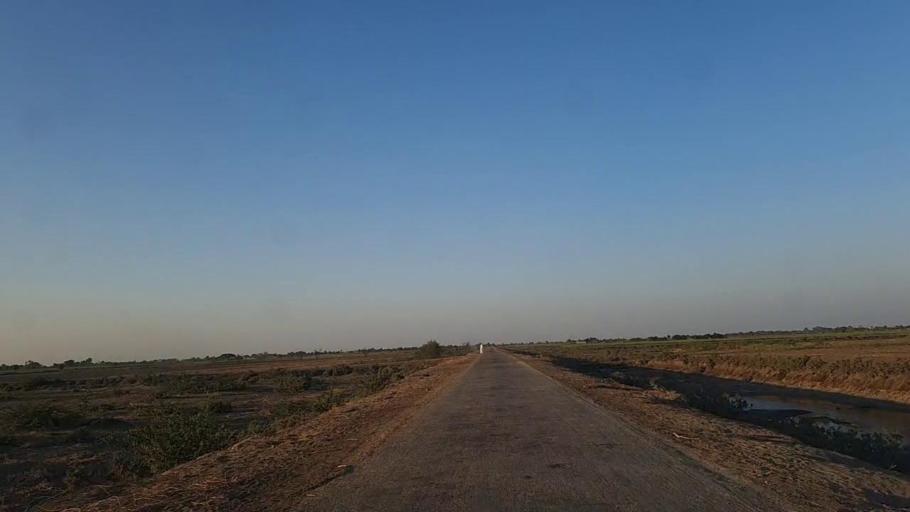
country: PK
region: Sindh
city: Naukot
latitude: 25.0170
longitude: 69.4168
